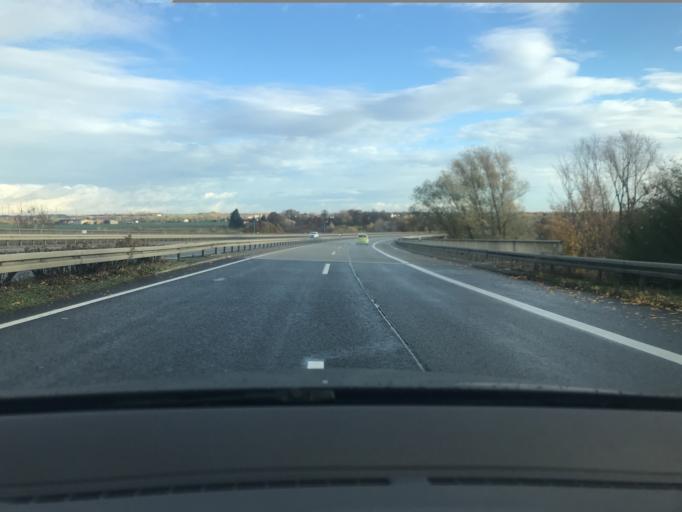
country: DE
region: Hesse
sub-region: Regierungsbezirk Darmstadt
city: Bad Vilbel
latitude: 50.1777
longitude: 8.7067
